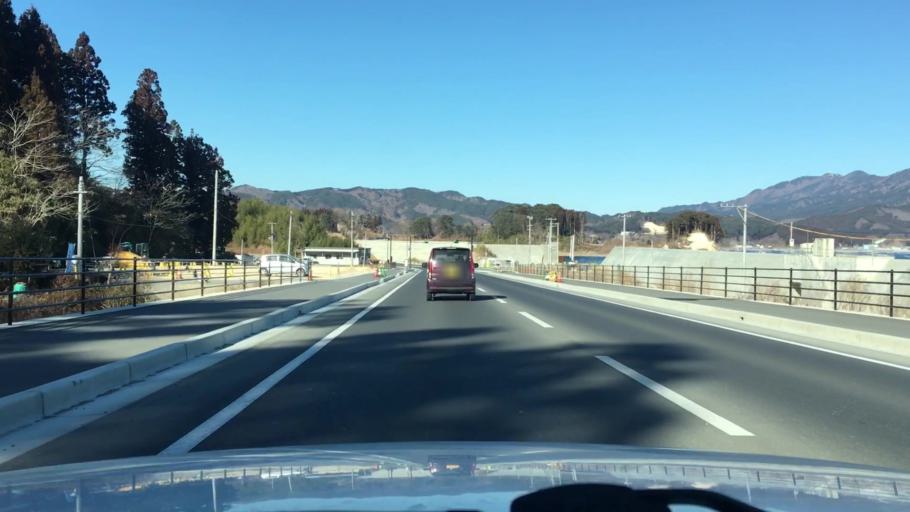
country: JP
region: Iwate
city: Yamada
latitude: 39.4519
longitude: 141.9615
